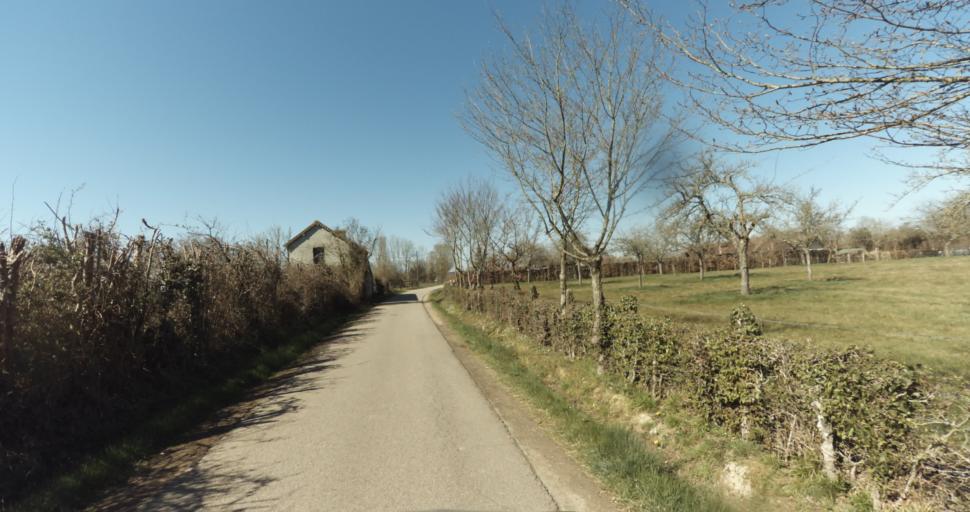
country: FR
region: Lower Normandy
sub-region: Departement du Calvados
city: Livarot
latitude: 48.9956
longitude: 0.1084
